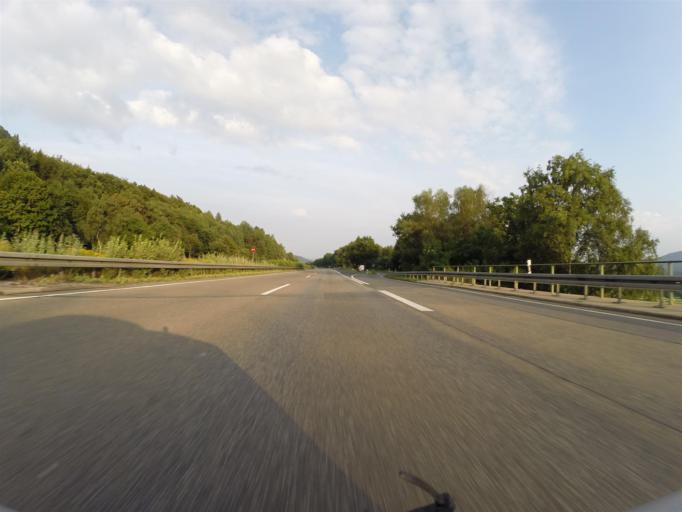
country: DE
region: Hesse
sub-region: Regierungsbezirk Kassel
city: Baunatal
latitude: 51.2854
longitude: 9.3674
